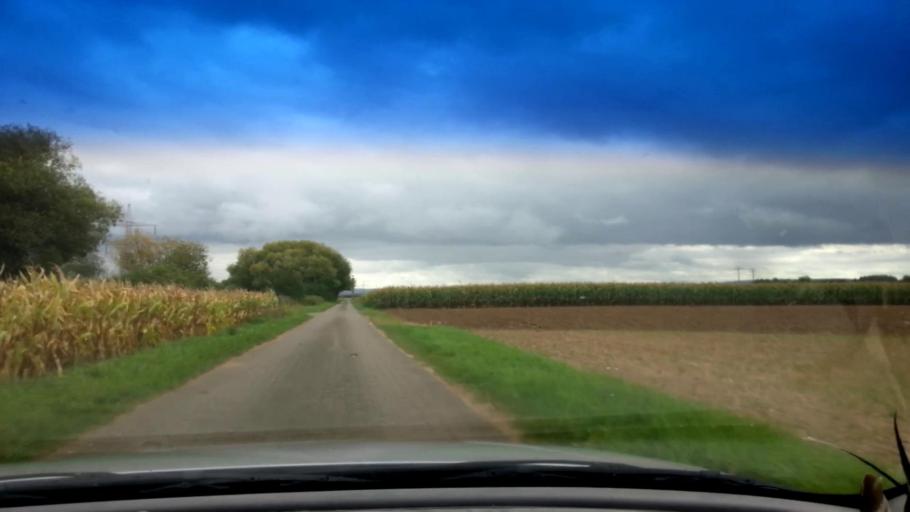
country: DE
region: Bavaria
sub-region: Upper Franconia
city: Viereth-Trunstadt
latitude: 49.9303
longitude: 10.7944
